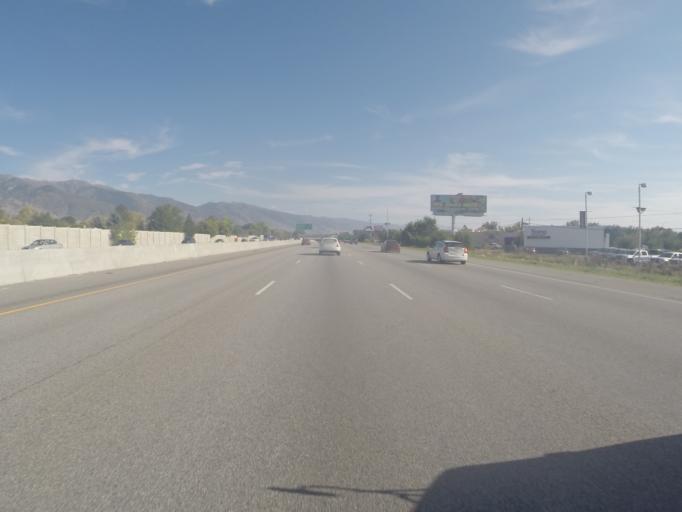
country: US
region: Utah
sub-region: Davis County
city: Layton
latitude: 41.0684
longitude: -111.9719
